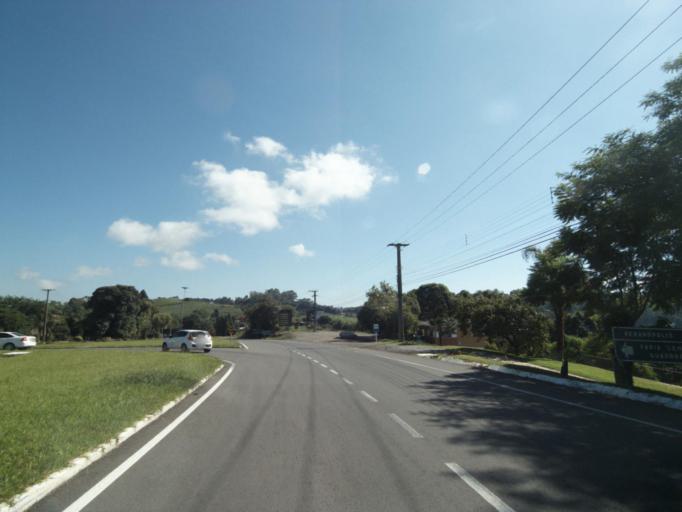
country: BR
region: Rio Grande do Sul
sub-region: Bento Goncalves
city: Bento Goncalves
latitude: -29.1197
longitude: -51.5423
